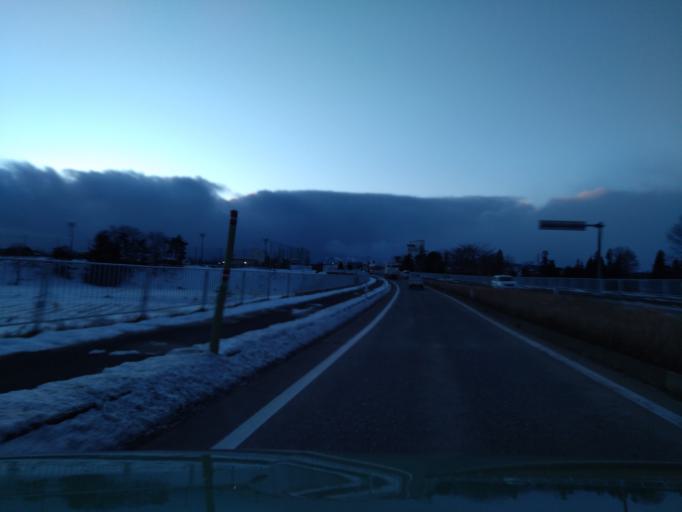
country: JP
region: Iwate
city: Shizukuishi
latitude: 39.7031
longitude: 140.9690
